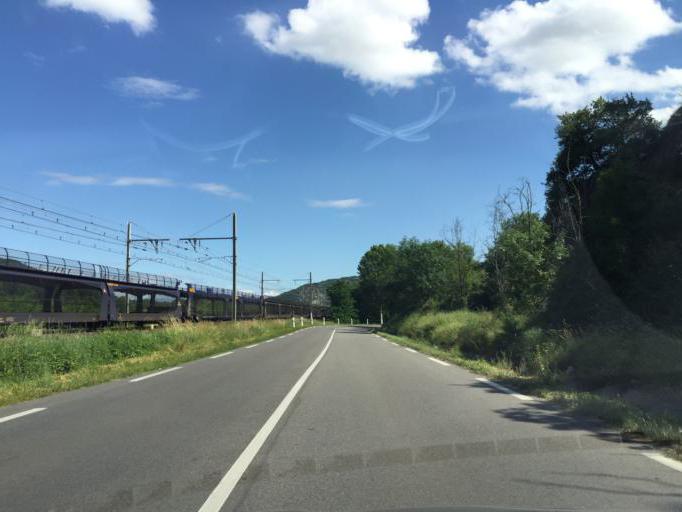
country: FR
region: Rhone-Alpes
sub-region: Departement de l'Ardeche
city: Saint-Jean-de-Muzols
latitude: 45.1062
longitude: 4.8141
